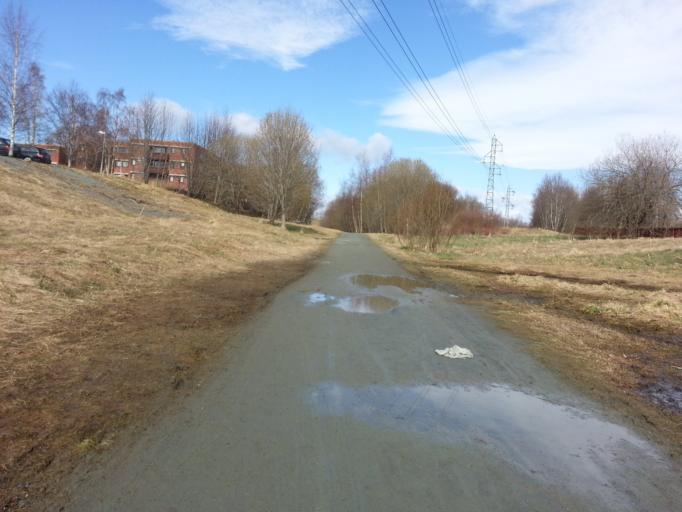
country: NO
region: Sor-Trondelag
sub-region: Trondheim
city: Trondheim
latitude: 63.4145
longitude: 10.4387
